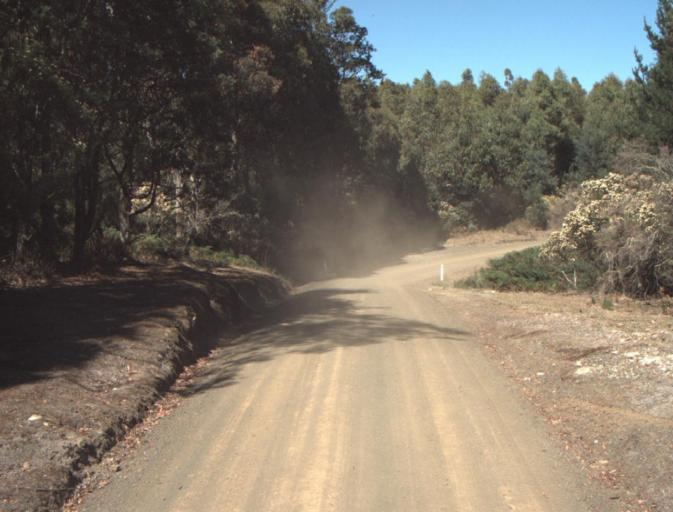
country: AU
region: Tasmania
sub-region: Dorset
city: Scottsdale
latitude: -41.2785
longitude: 147.3419
